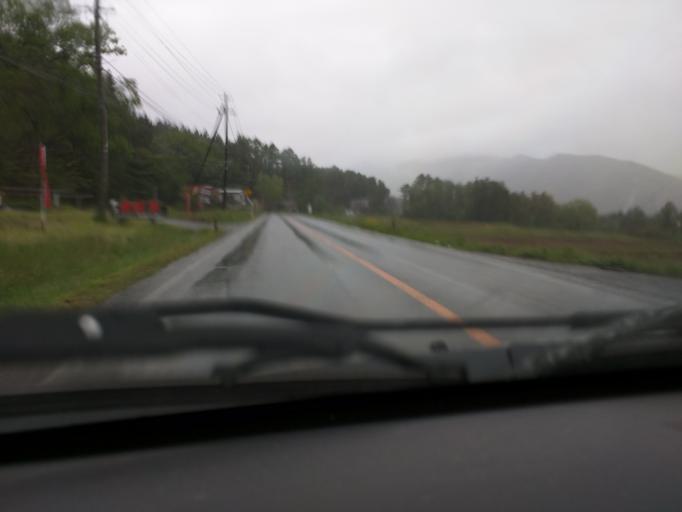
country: JP
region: Fukushima
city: Inawashiro
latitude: 37.5898
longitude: 140.1254
